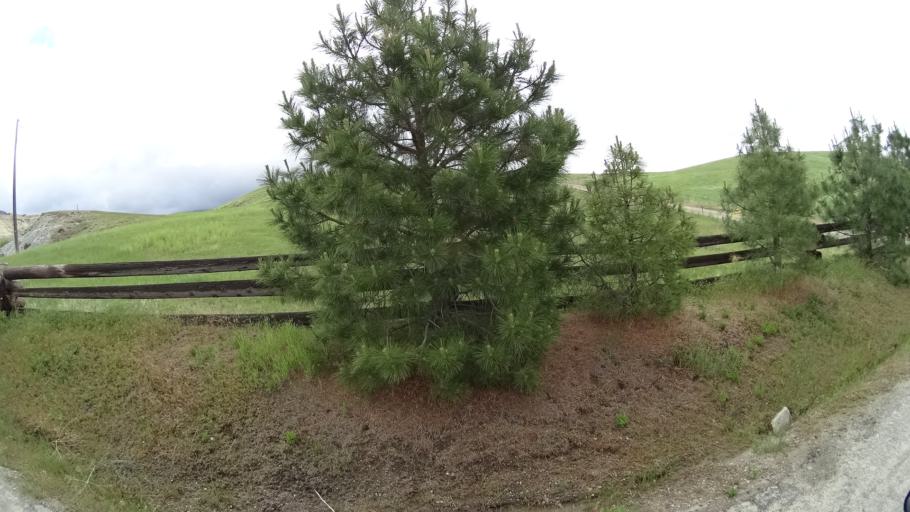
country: US
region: Idaho
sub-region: Ada County
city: Garden City
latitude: 43.7409
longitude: -116.2254
